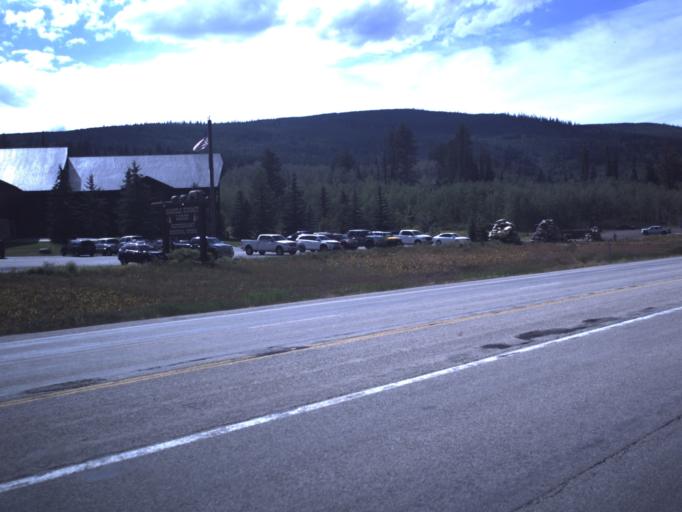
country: US
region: Utah
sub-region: Wasatch County
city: Heber
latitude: 40.3019
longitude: -111.2558
